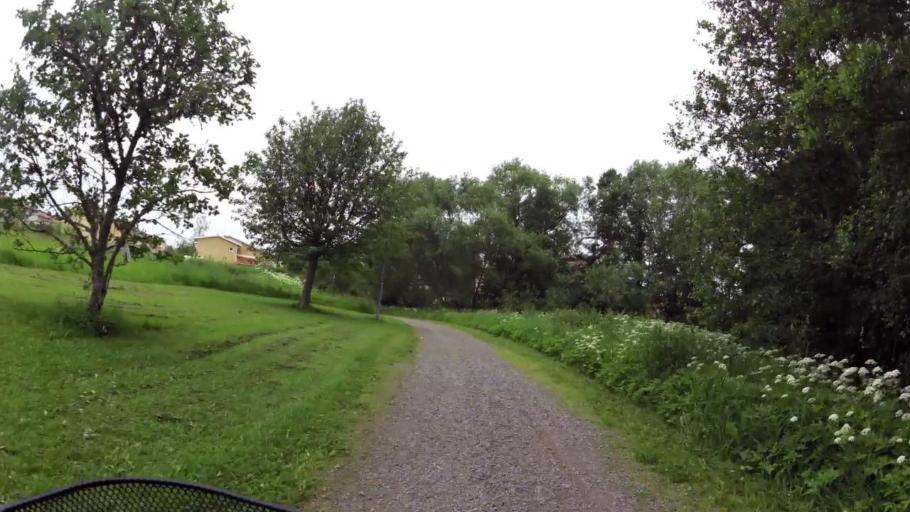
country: SE
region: OEstergoetland
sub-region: Linkopings Kommun
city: Linkoping
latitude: 58.3716
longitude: 15.6629
